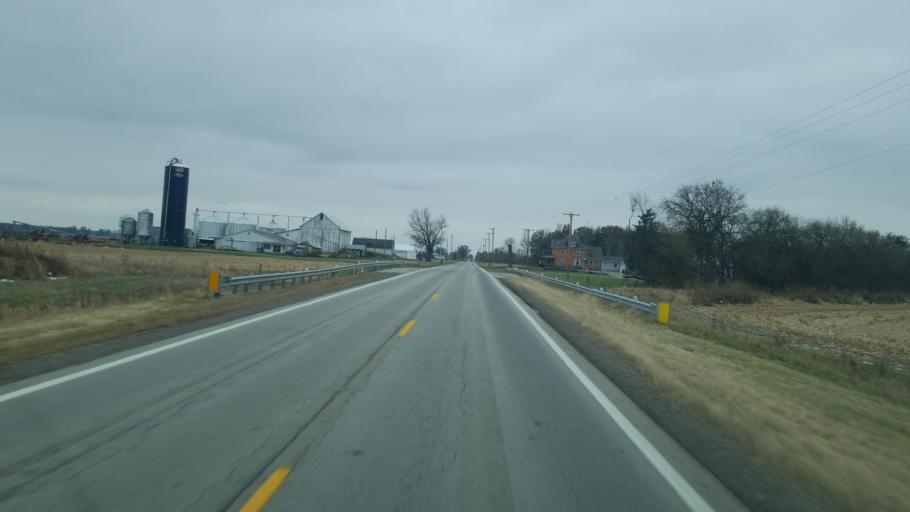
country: US
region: Ohio
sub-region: Huron County
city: Bellevue
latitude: 41.2364
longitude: -82.8080
